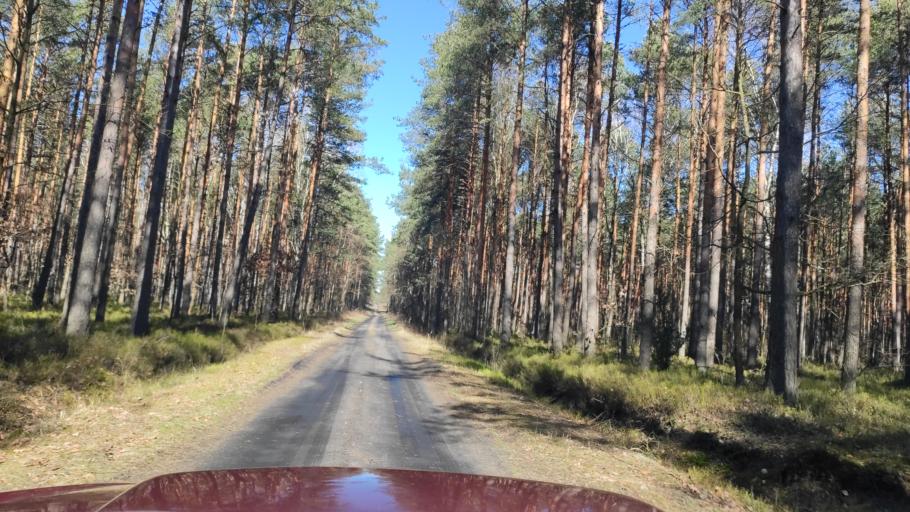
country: PL
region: Masovian Voivodeship
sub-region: Powiat zwolenski
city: Zwolen
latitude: 51.4095
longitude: 21.5572
